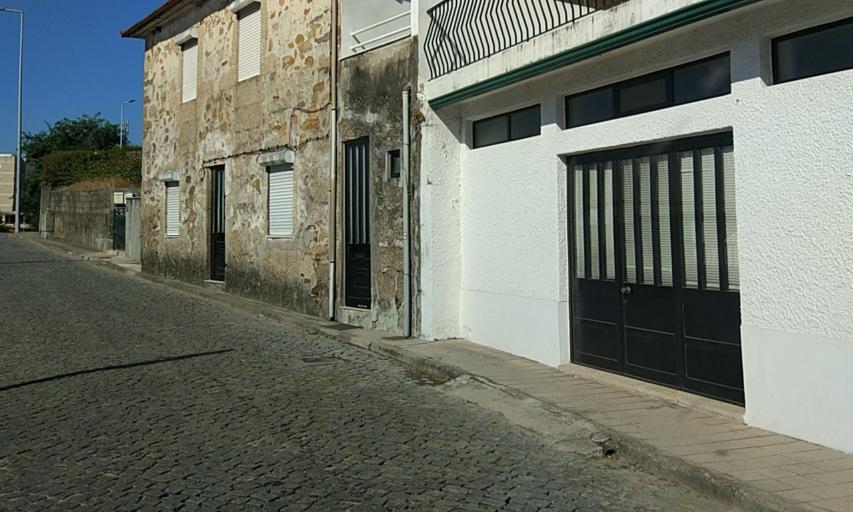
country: PT
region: Porto
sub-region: Santo Tirso
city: Santo Tirso
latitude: 41.3445
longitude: -8.4828
